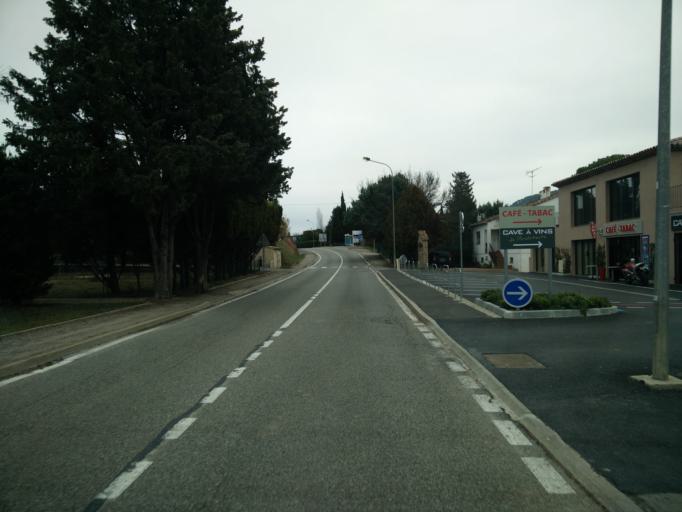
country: FR
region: Provence-Alpes-Cote d'Azur
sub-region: Departement du Var
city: Salernes
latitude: 43.5596
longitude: 6.2473
